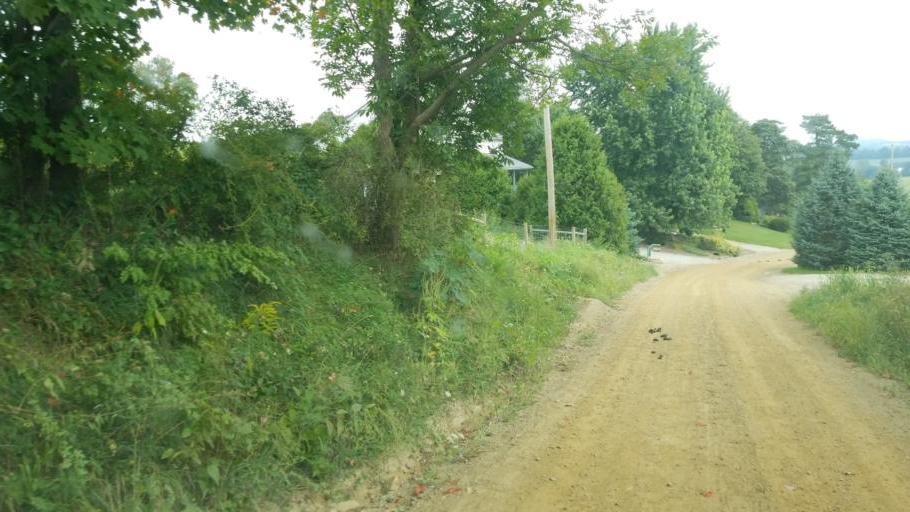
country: US
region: Ohio
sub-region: Knox County
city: Danville
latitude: 40.4889
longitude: -82.2992
